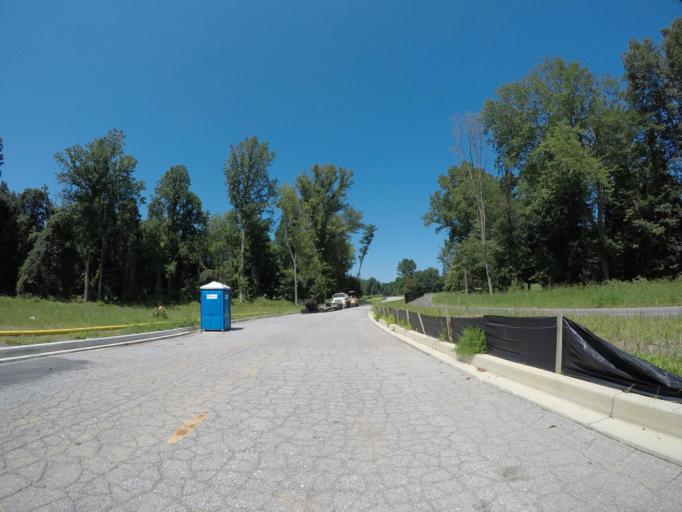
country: US
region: Maryland
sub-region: Howard County
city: Columbia
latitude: 39.2980
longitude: -76.8696
